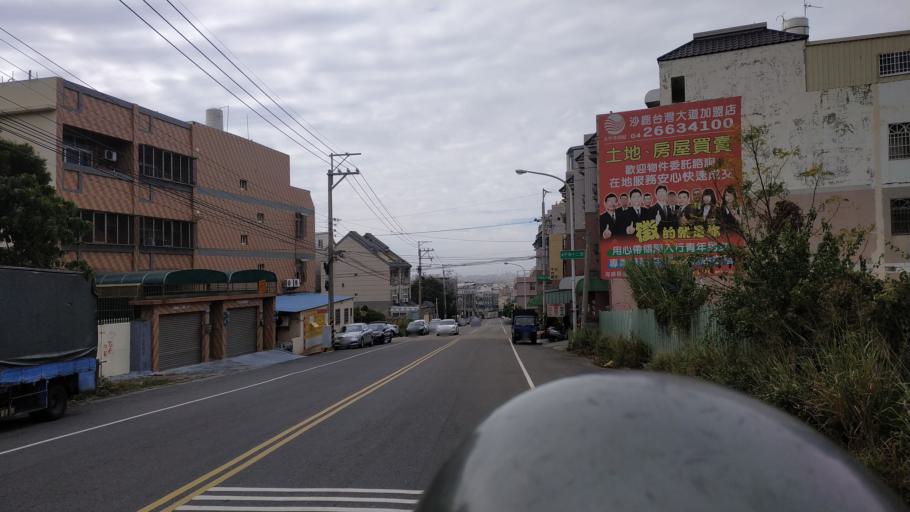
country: TW
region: Taiwan
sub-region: Taichung City
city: Taichung
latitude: 24.2186
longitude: 120.5780
